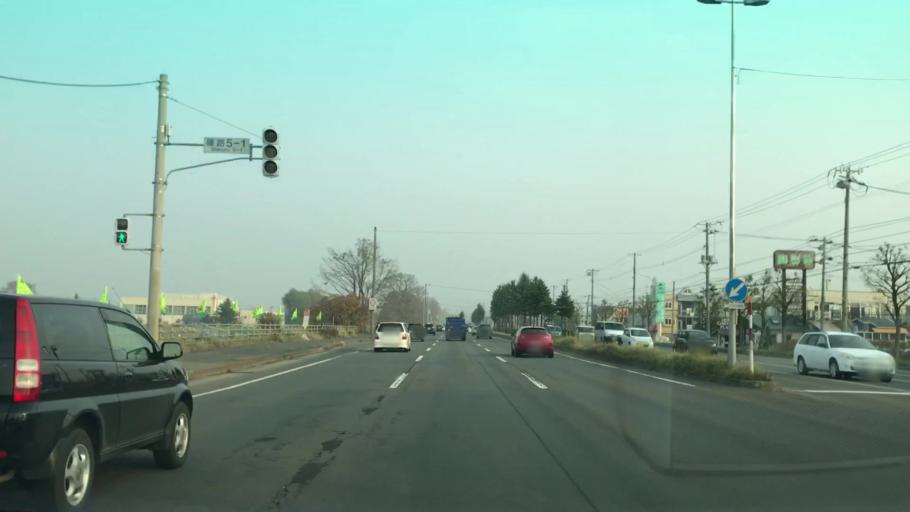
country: JP
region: Hokkaido
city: Sapporo
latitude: 43.1503
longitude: 141.3509
